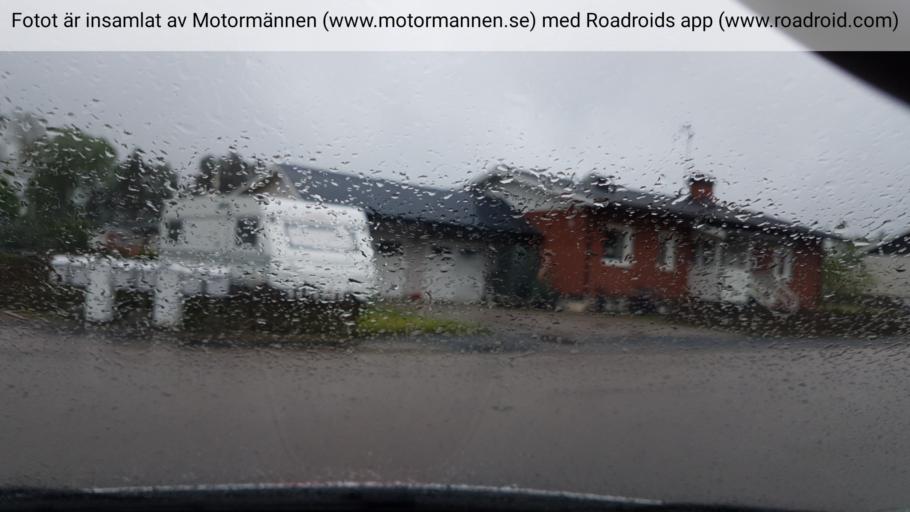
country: SE
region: Vaestra Goetaland
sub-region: Ulricehamns Kommun
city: Ulricehamn
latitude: 57.8595
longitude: 13.4354
